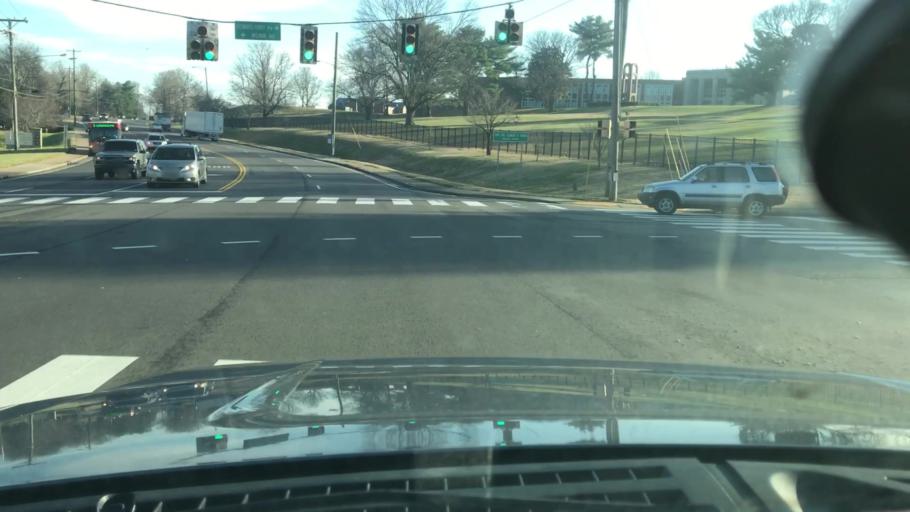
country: US
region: Tennessee
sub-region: Davidson County
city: Lakewood
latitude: 36.1683
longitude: -86.6570
